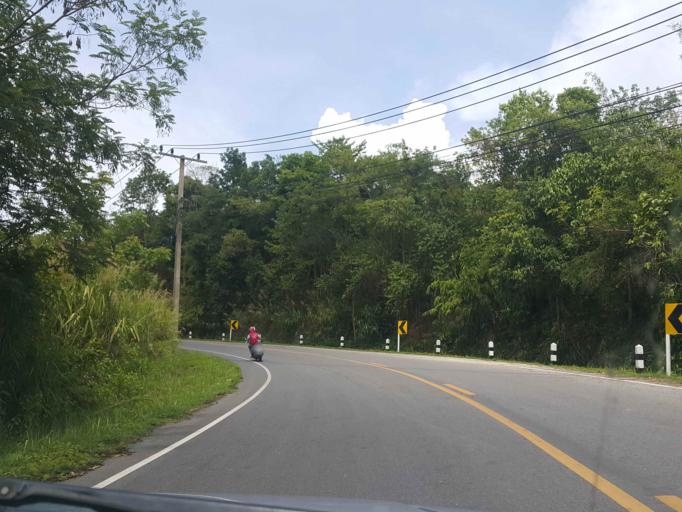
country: TH
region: Nan
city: Ban Luang
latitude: 18.8619
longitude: 100.4605
